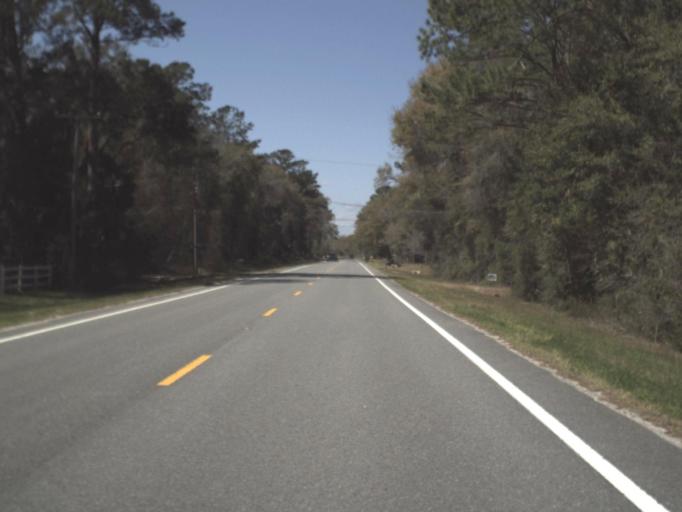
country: US
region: Florida
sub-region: Leon County
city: Woodville
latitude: 30.2370
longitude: -84.2526
